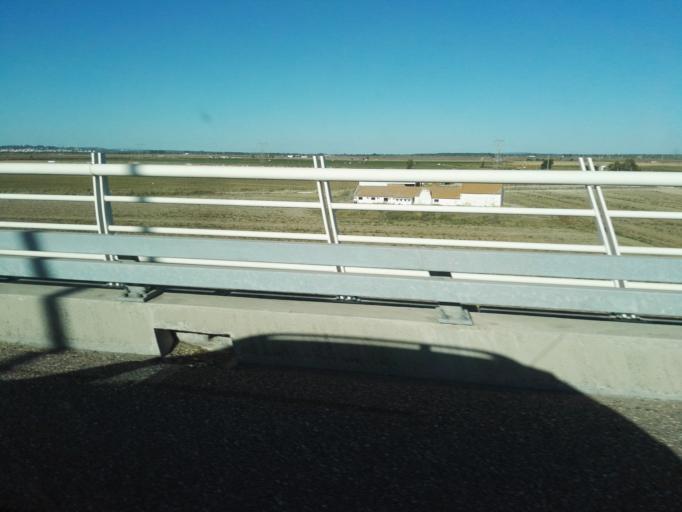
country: PT
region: Santarem
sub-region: Benavente
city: Samora Correia
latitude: 38.9923
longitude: -8.8960
